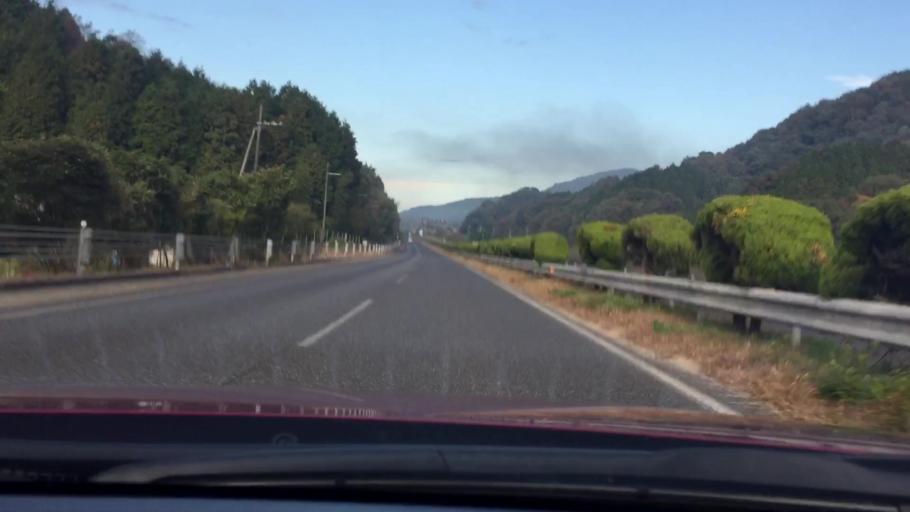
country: JP
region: Hyogo
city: Yamazakicho-nakabirose
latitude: 34.9705
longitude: 134.6672
